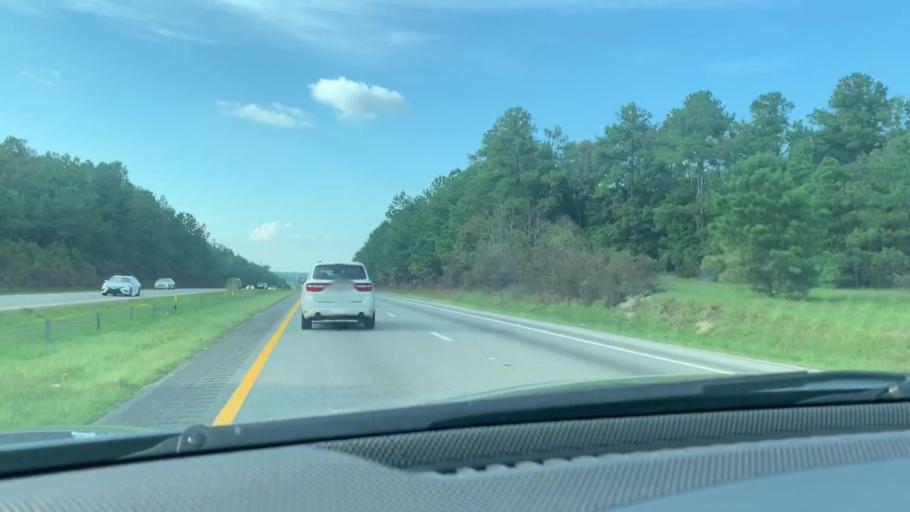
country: US
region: South Carolina
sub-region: Calhoun County
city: Oak Grove
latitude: 33.7392
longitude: -80.9370
